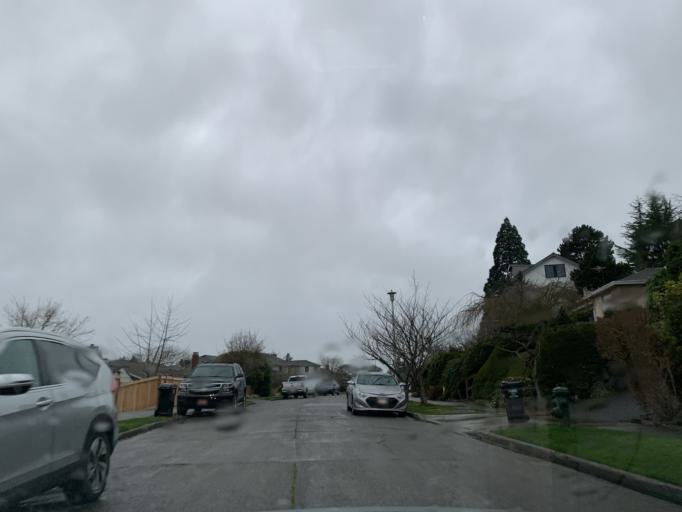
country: US
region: Washington
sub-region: King County
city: Yarrow Point
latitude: 47.6710
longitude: -122.2737
